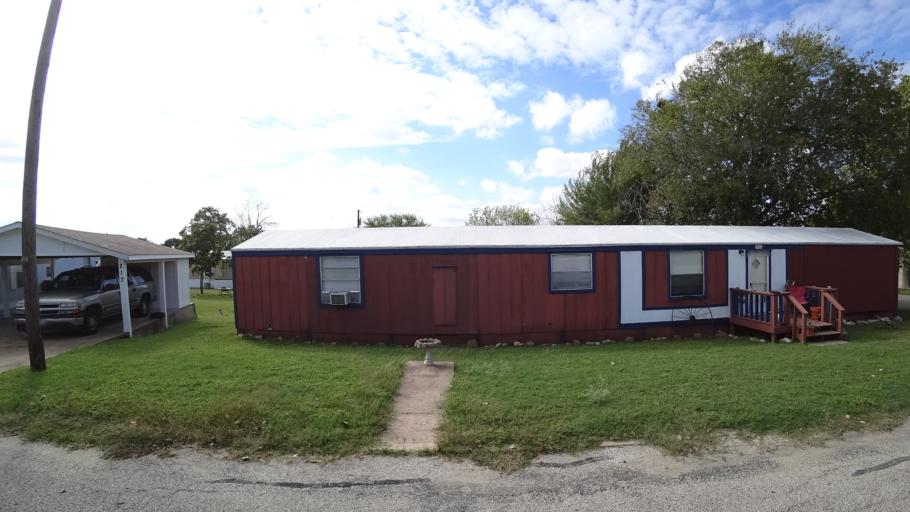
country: US
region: Texas
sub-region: Travis County
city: Pflugerville
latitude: 30.4351
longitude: -97.6424
